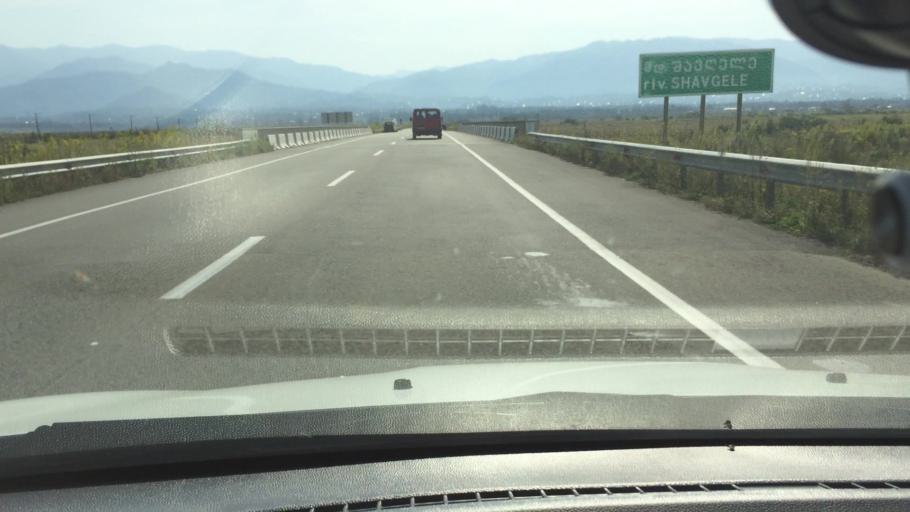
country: GE
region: Ajaria
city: Ochkhamuri
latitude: 41.8787
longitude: 41.8216
